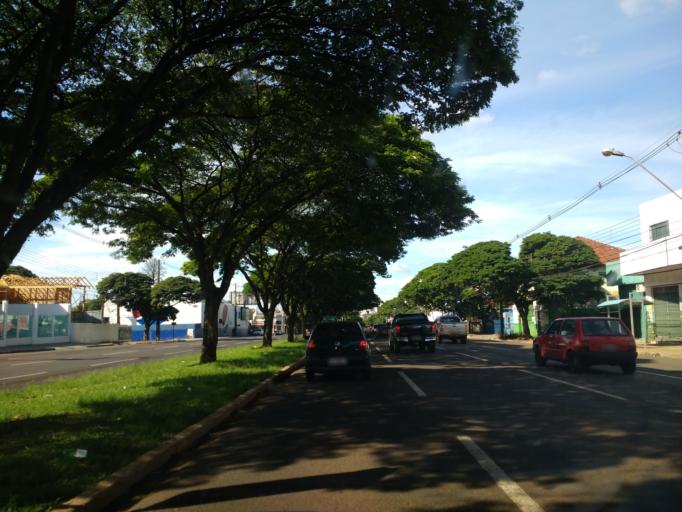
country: BR
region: Parana
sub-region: Maringa
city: Maringa
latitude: -23.4165
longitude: -51.9563
